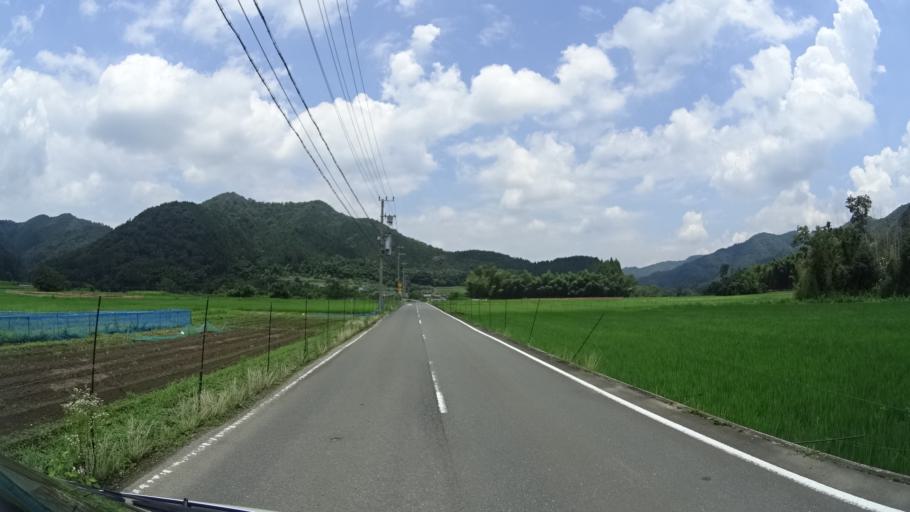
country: JP
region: Kyoto
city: Ayabe
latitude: 35.1999
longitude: 135.2445
